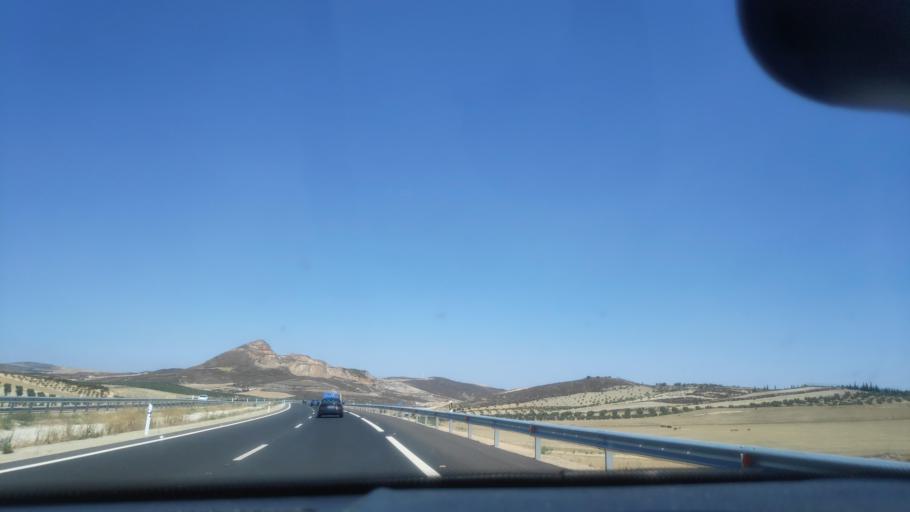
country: ES
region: Andalusia
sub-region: Provincia de Granada
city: Alhendin
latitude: 37.0882
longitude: -3.6677
